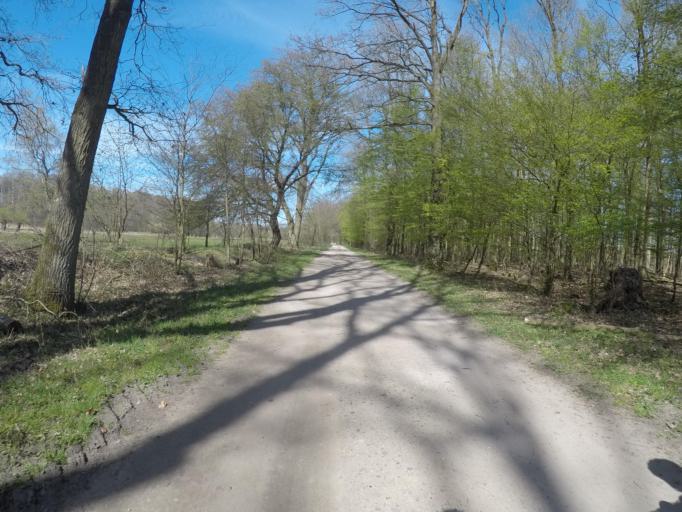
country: DE
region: Schleswig-Holstein
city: Jersbek
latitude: 53.7262
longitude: 10.1789
